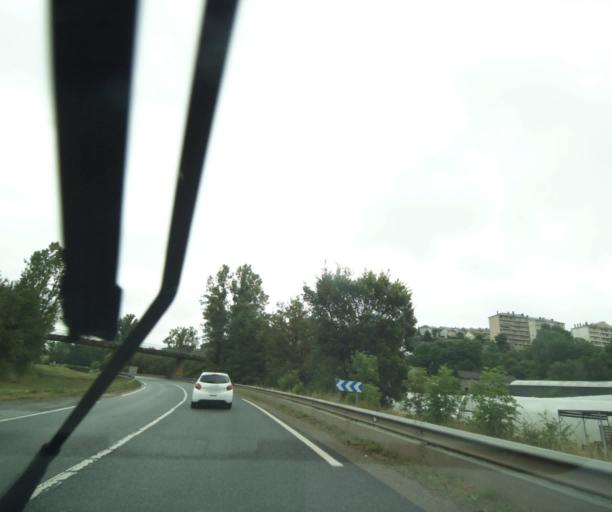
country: FR
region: Midi-Pyrenees
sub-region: Departement de l'Aveyron
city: Rodez
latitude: 44.3573
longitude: 2.5642
